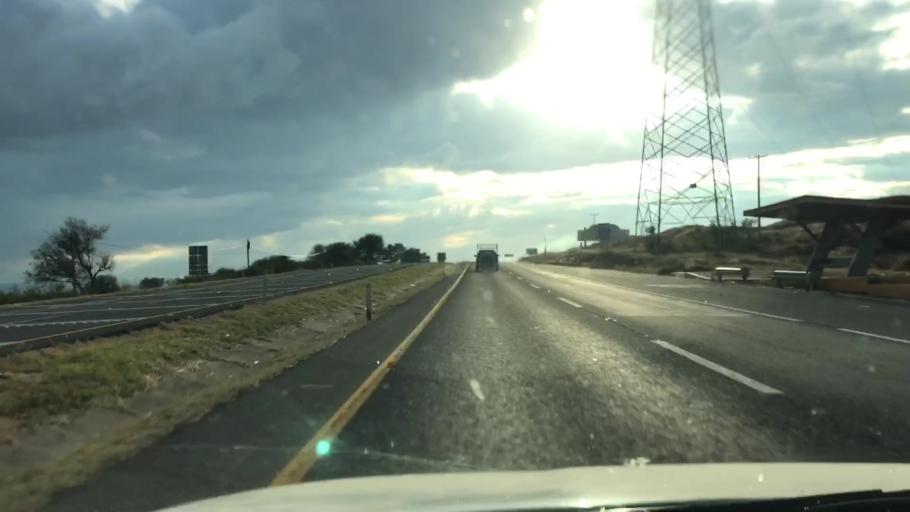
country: MX
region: Guanajuato
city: Penjamo
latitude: 20.3991
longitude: -101.7518
